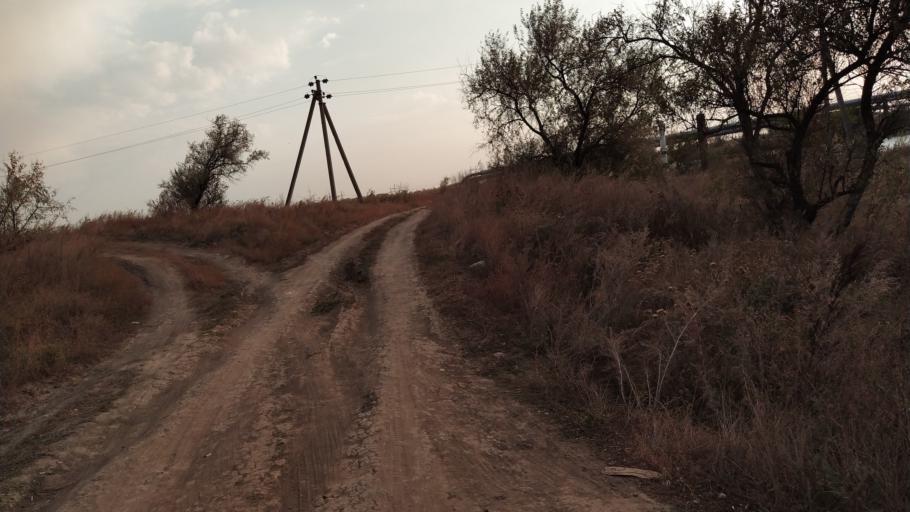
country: RU
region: Rostov
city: Kuleshovka
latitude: 47.1169
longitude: 39.6014
